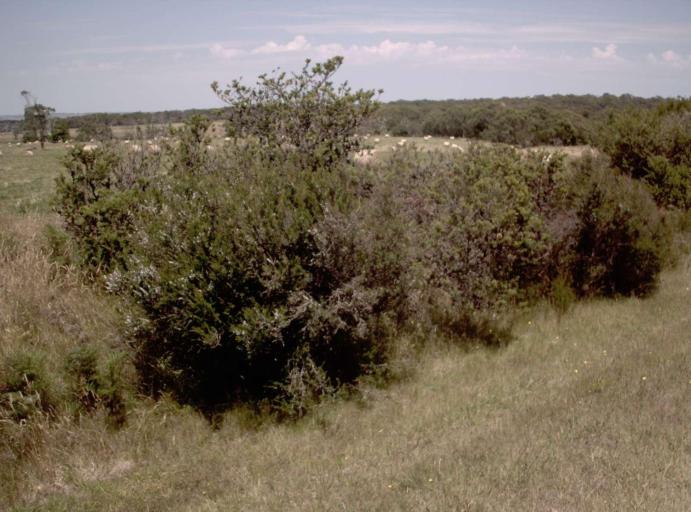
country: AU
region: Victoria
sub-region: Bass Coast
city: North Wonthaggi
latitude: -38.6693
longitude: 145.9204
